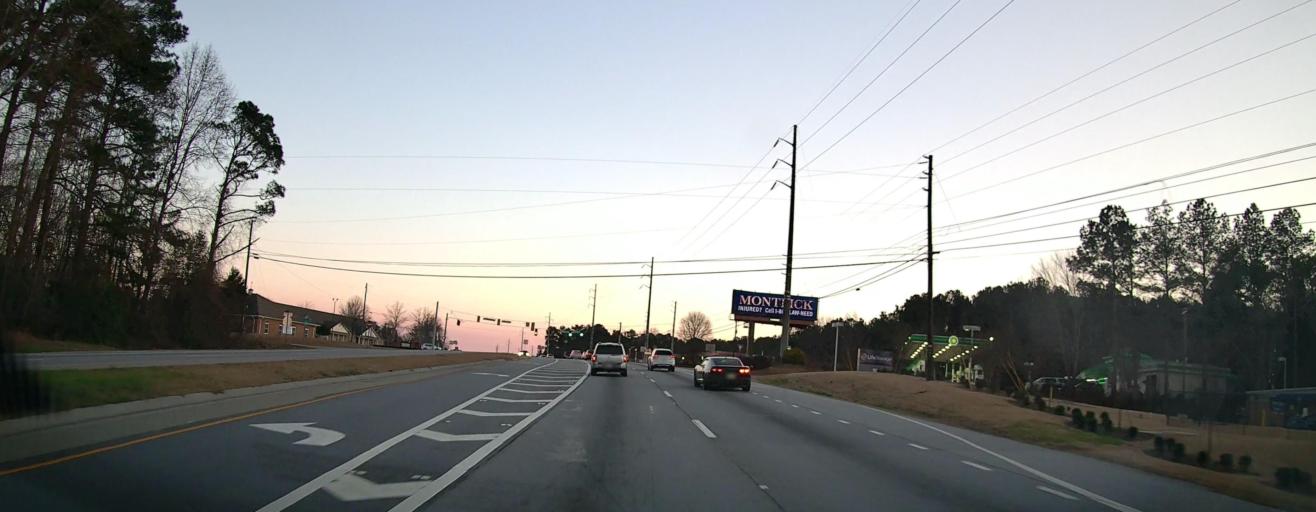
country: US
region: Georgia
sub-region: Clayton County
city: Riverdale
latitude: 33.5109
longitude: -84.4300
